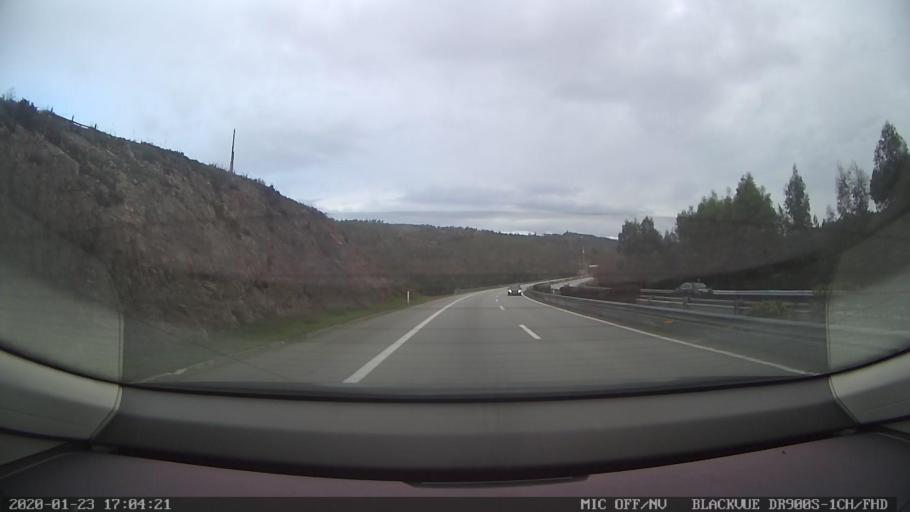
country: PT
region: Porto
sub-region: Paredes
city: Recarei
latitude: 41.1750
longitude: -8.4186
